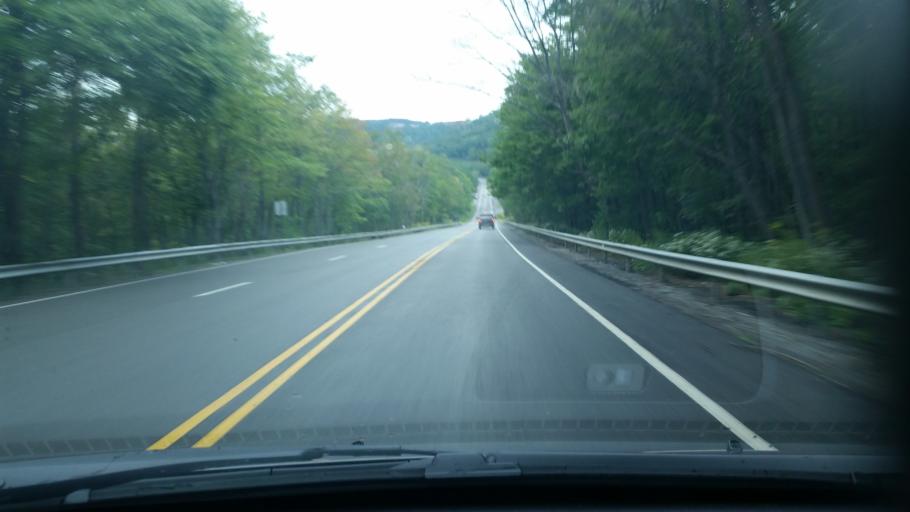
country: US
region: Pennsylvania
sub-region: Clearfield County
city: Shiloh
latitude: 41.0703
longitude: -78.3239
